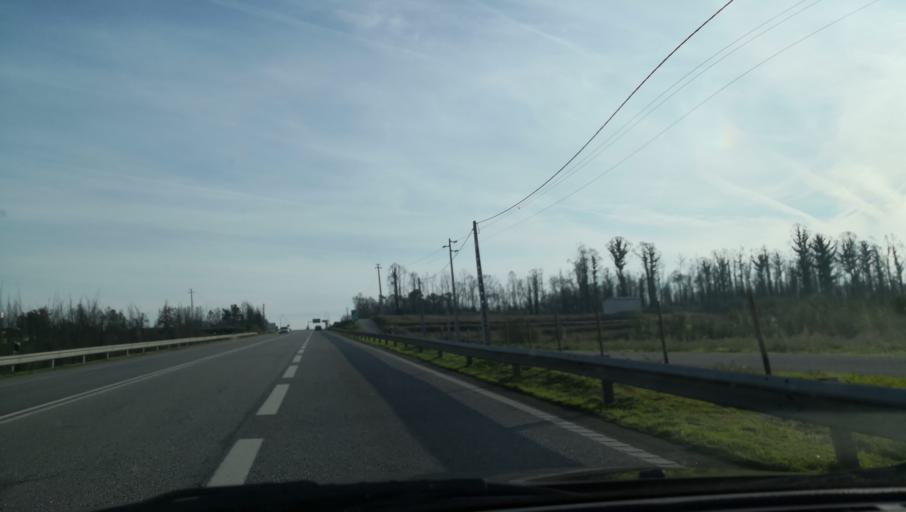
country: PT
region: Viseu
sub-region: Concelho de Tondela
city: Tondela
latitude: 40.5073
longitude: -8.0852
